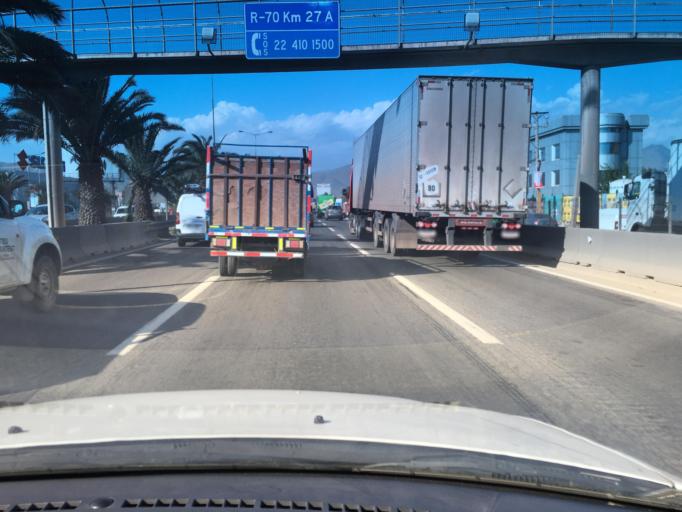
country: CL
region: Santiago Metropolitan
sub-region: Provincia de Santiago
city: Lo Prado
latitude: -33.3710
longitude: -70.7080
